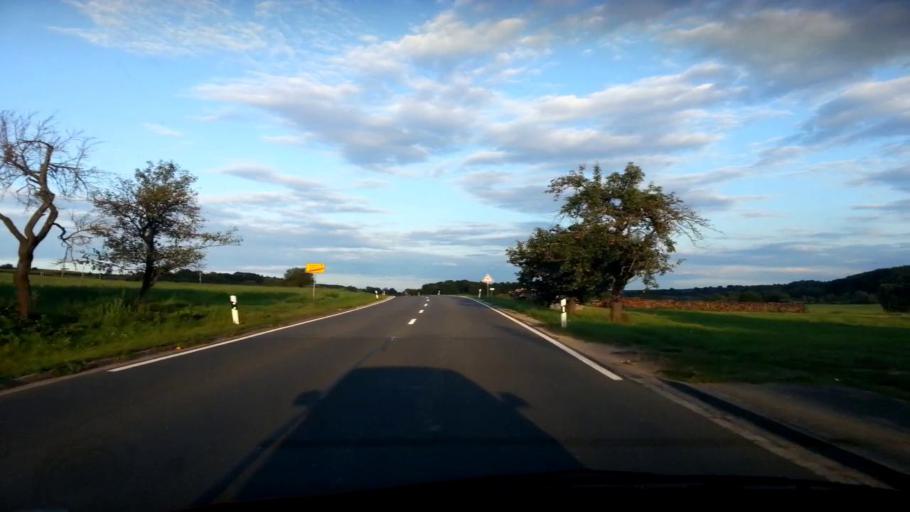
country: DE
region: Bavaria
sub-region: Upper Franconia
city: Burgwindheim
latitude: 49.8232
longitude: 10.6380
